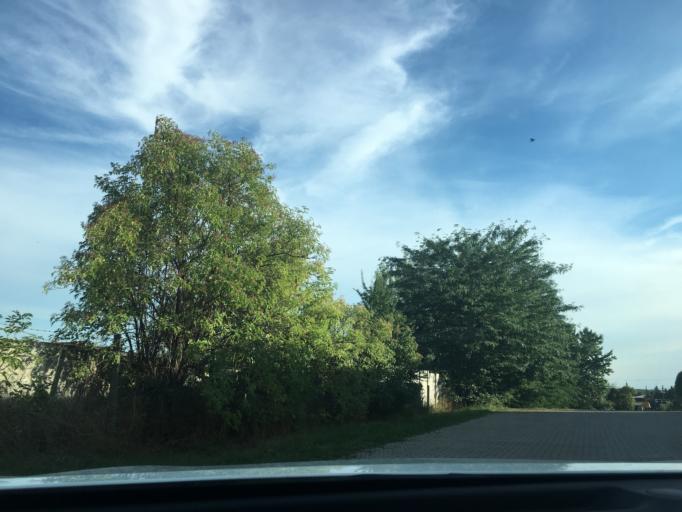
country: HU
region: Budapest
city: Budapest XVII. keruelet
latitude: 47.4687
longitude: 19.2833
